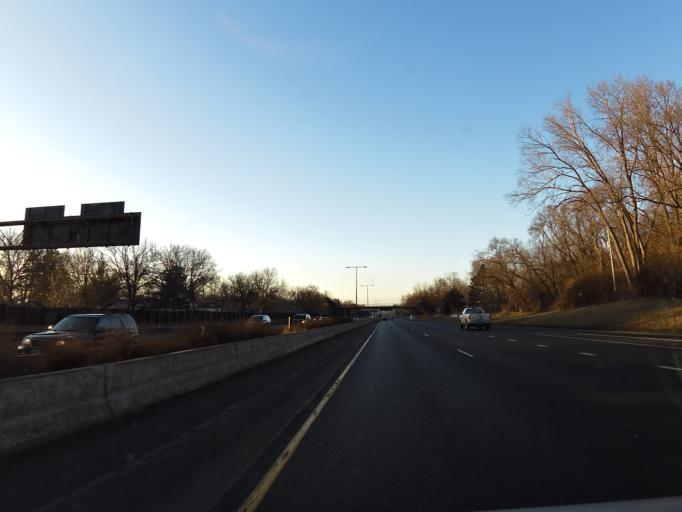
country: US
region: Minnesota
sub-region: Dakota County
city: Mendota Heights
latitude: 44.9241
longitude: -93.1451
